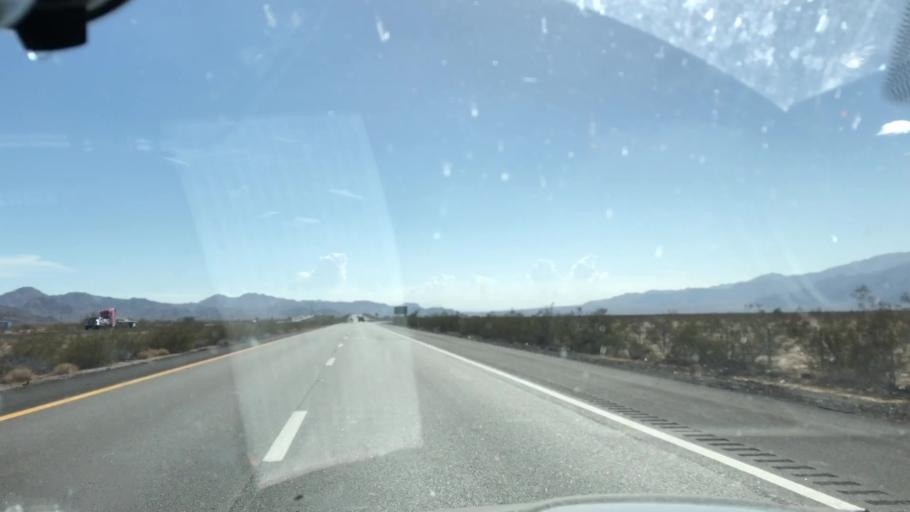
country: US
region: California
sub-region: Imperial County
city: Niland
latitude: 33.6789
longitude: -115.5583
